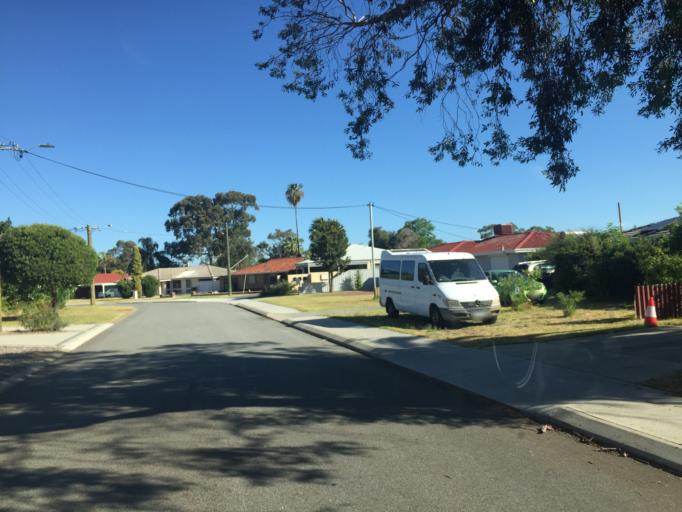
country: AU
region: Western Australia
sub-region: Canning
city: East Cannington
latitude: -32.0137
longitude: 115.9668
